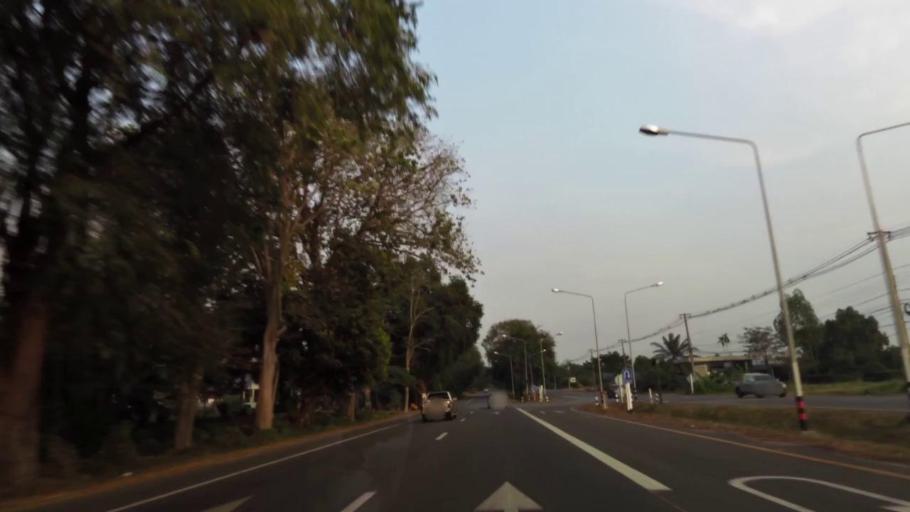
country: TH
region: Chanthaburi
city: Khlung
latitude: 12.4654
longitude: 102.2080
